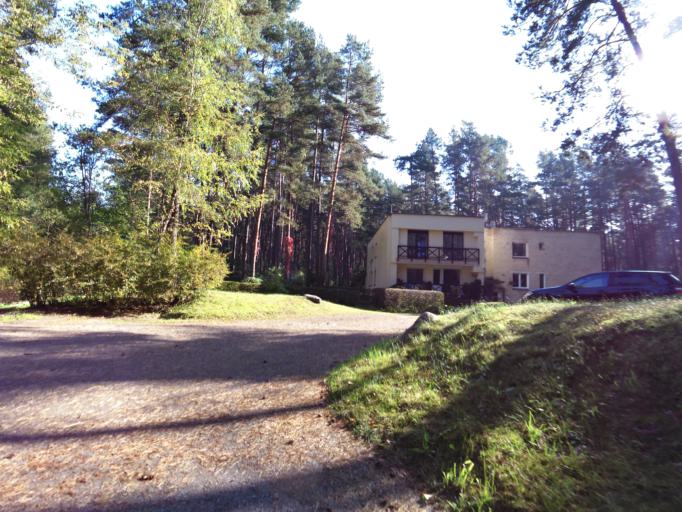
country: LT
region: Vilnius County
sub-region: Vilnius
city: Vilnius
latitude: 54.7355
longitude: 25.3034
